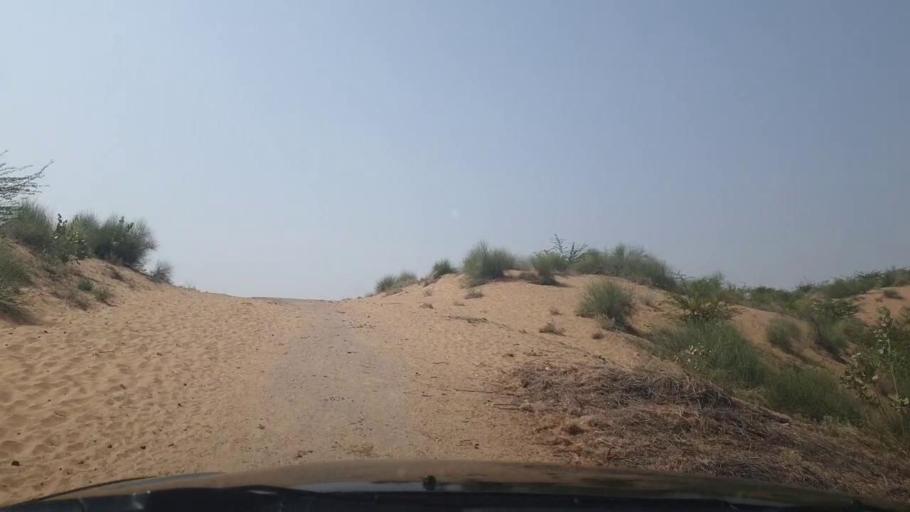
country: PK
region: Sindh
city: Islamkot
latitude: 25.0784
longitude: 70.3063
